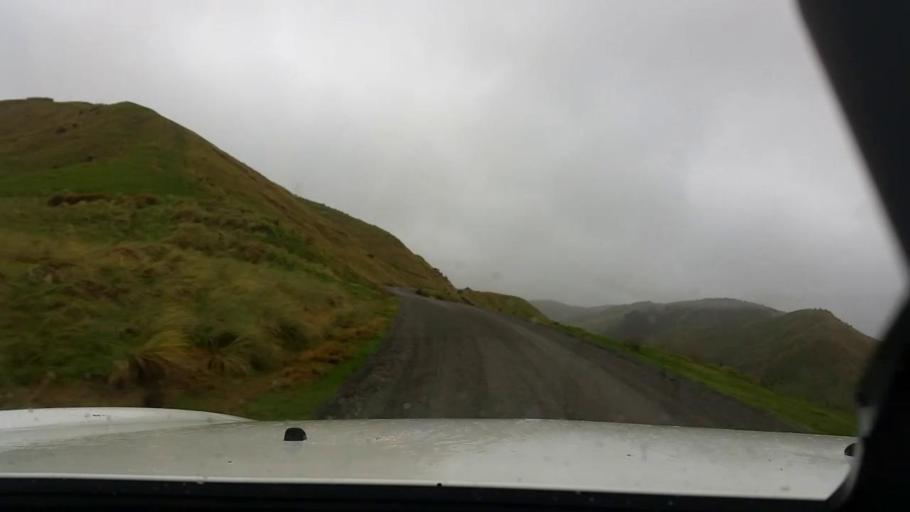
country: NZ
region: Wellington
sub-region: Masterton District
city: Masterton
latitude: -41.2509
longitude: 175.9147
